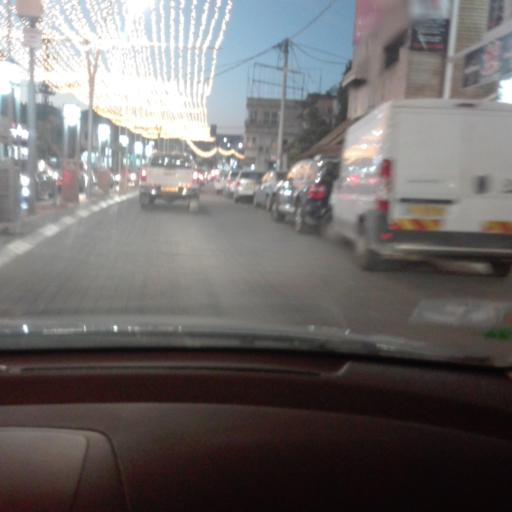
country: PS
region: West Bank
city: Nazlat `Isa
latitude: 32.4151
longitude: 35.0461
